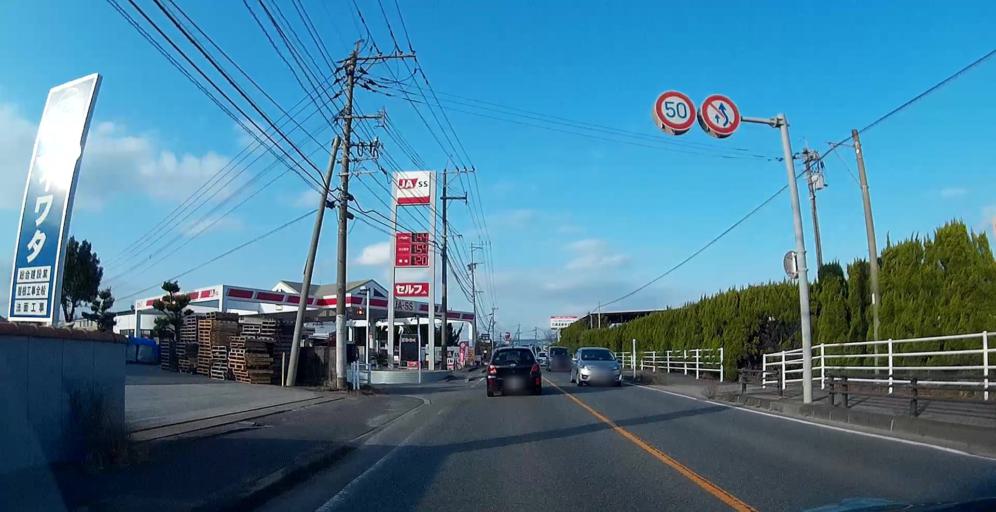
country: JP
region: Kumamoto
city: Matsubase
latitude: 32.6021
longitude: 130.7022
